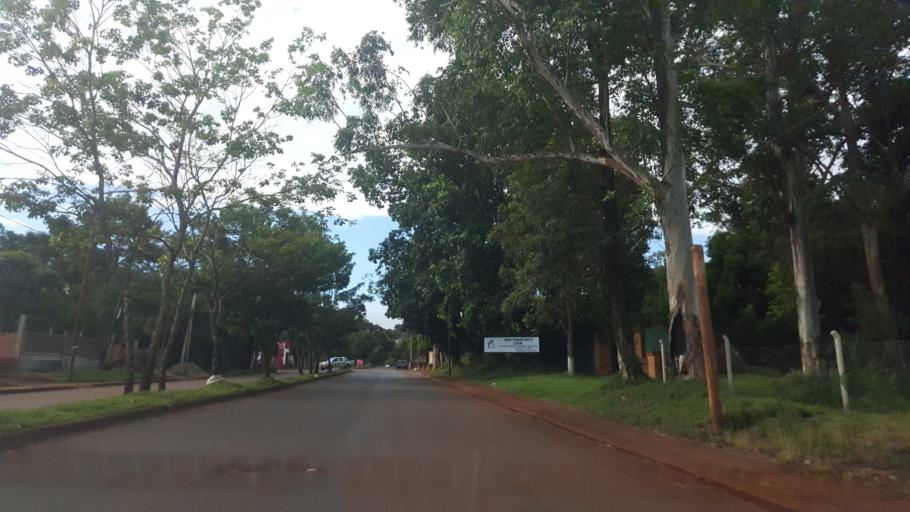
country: AR
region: Misiones
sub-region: Departamento de Capital
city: Posadas
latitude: -27.3915
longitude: -55.9350
